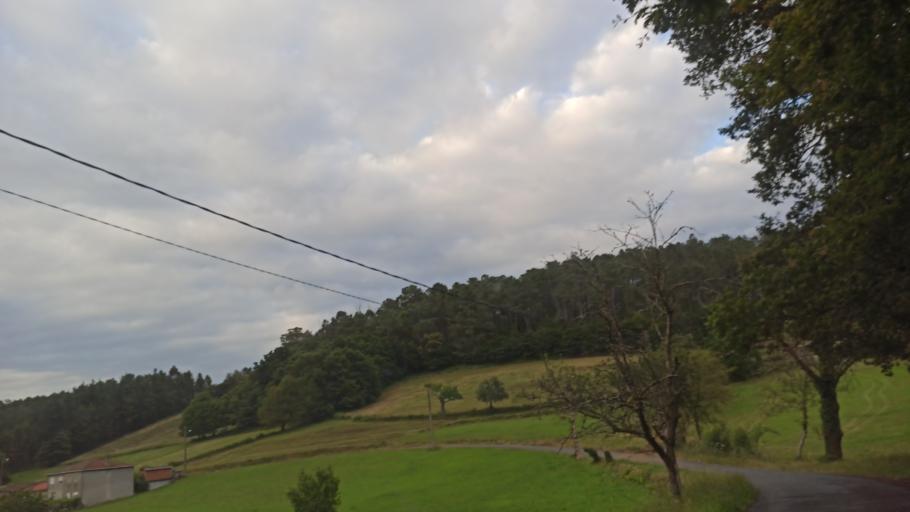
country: ES
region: Galicia
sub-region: Provincia da Coruna
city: Santiso
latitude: 42.8339
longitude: -8.1229
